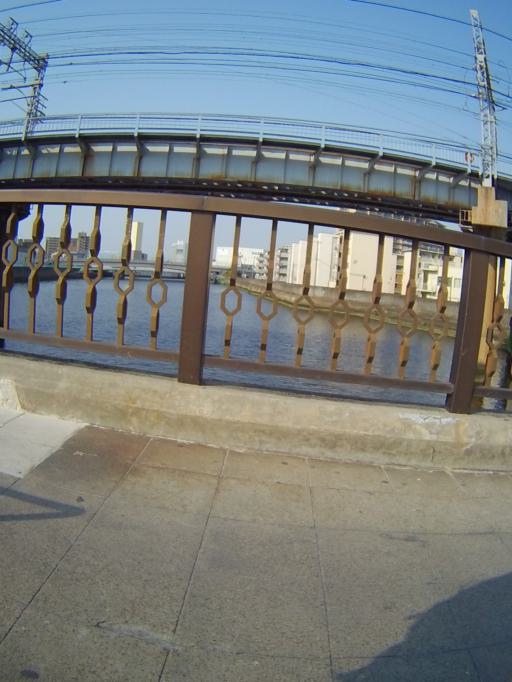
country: JP
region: Osaka
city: Osaka-shi
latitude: 34.6841
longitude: 135.4632
